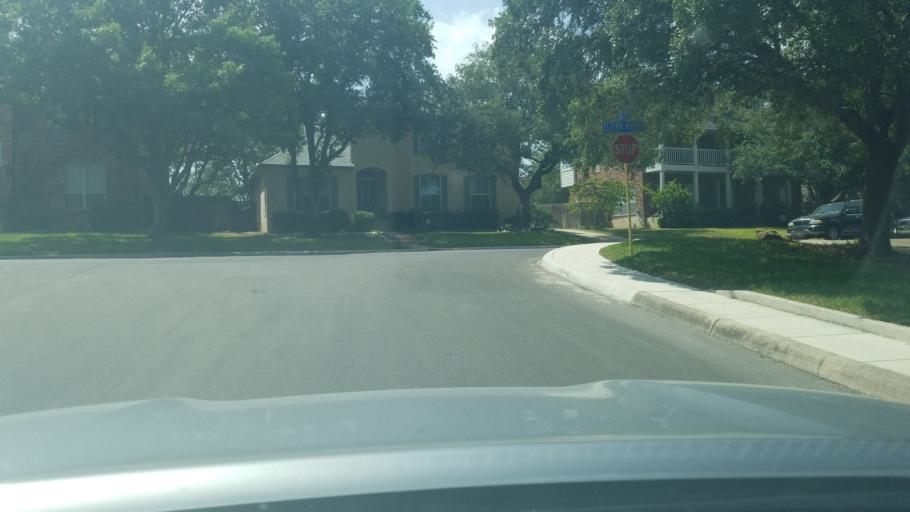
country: US
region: Texas
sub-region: Bexar County
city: Hollywood Park
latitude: 29.6429
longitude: -98.4969
